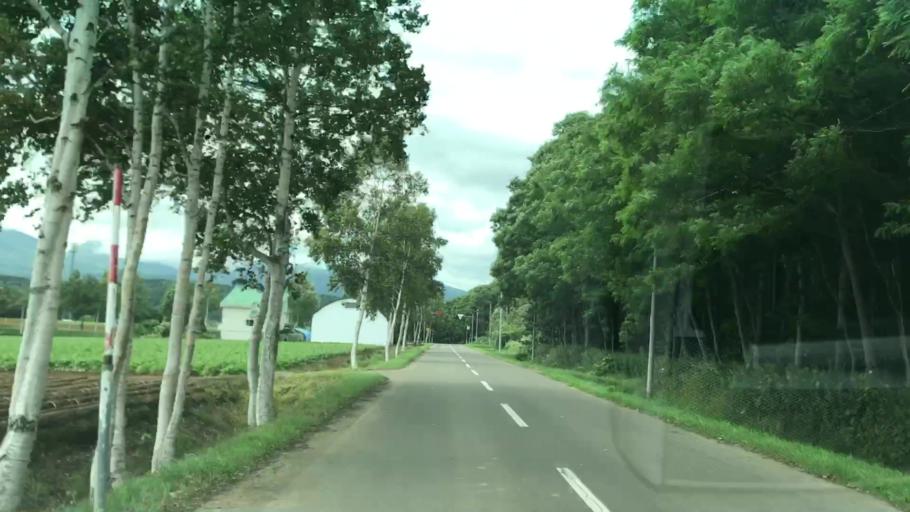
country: JP
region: Hokkaido
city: Niseko Town
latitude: 42.9136
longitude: 140.7626
